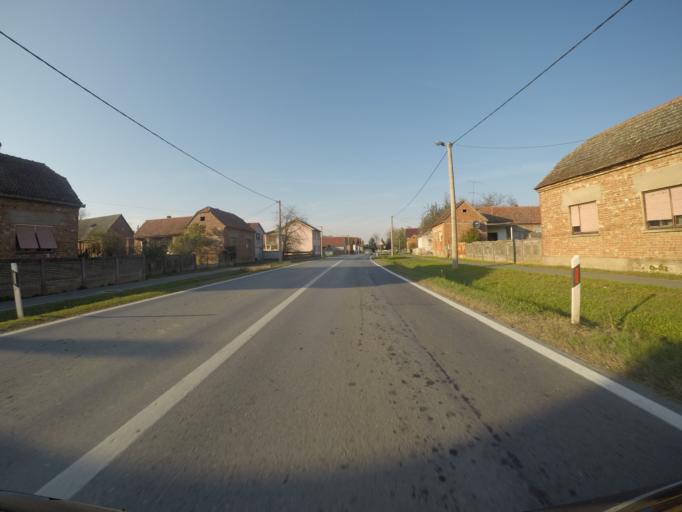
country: HU
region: Somogy
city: Barcs
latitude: 45.9073
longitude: 17.4412
